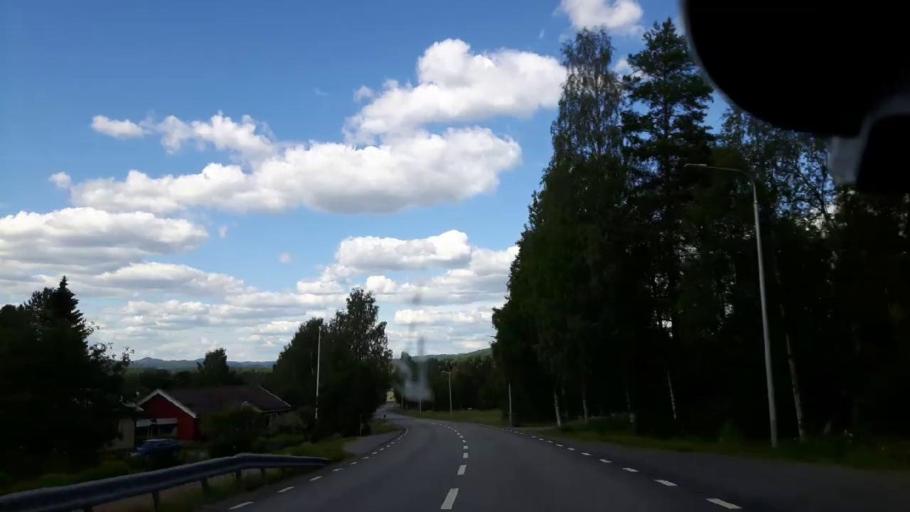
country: SE
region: Jaemtland
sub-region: Ragunda Kommun
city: Hammarstrand
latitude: 63.0040
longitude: 16.6729
